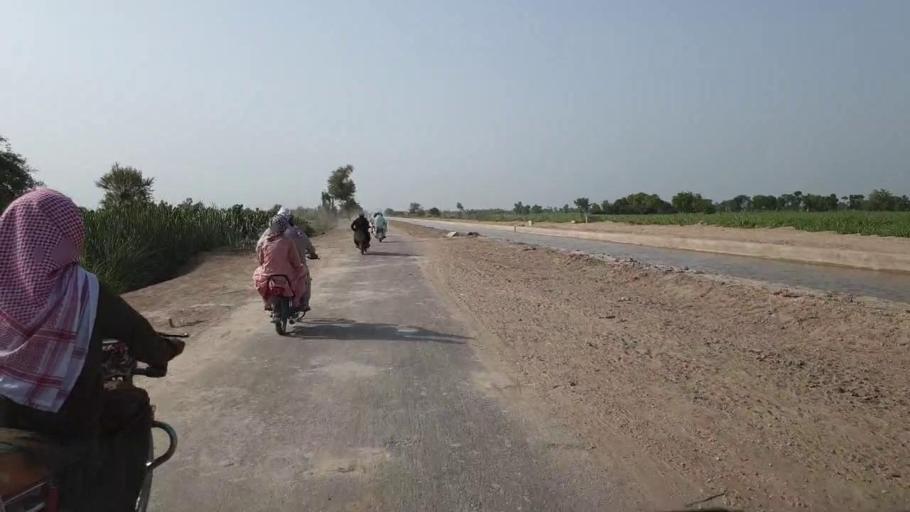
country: PK
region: Sindh
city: Daur
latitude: 26.3367
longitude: 68.1637
